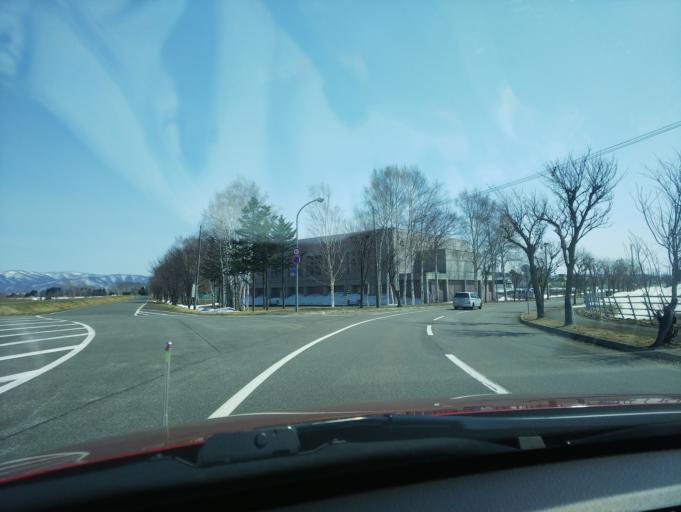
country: JP
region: Hokkaido
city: Nayoro
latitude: 44.1904
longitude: 142.3948
